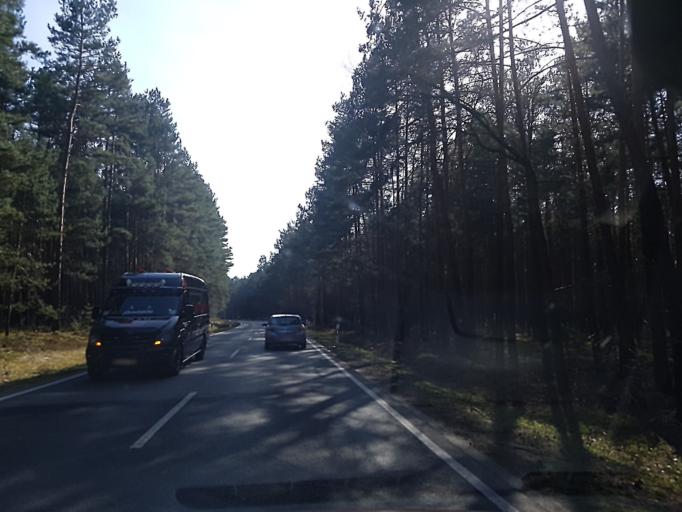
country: DE
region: Brandenburg
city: Calau
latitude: 51.7165
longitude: 13.9228
